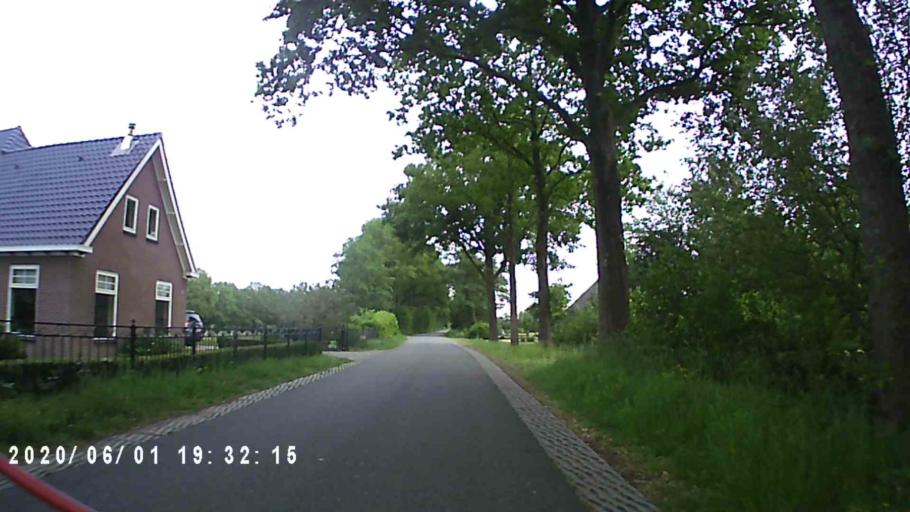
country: NL
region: Friesland
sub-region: Gemeente Achtkarspelen
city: Augustinusga
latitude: 53.2123
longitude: 6.1574
